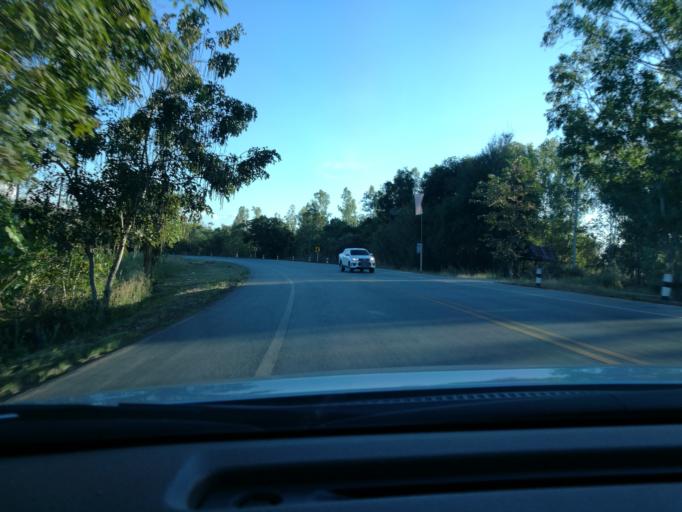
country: TH
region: Phitsanulok
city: Nakhon Thai
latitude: 17.0454
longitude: 100.8092
